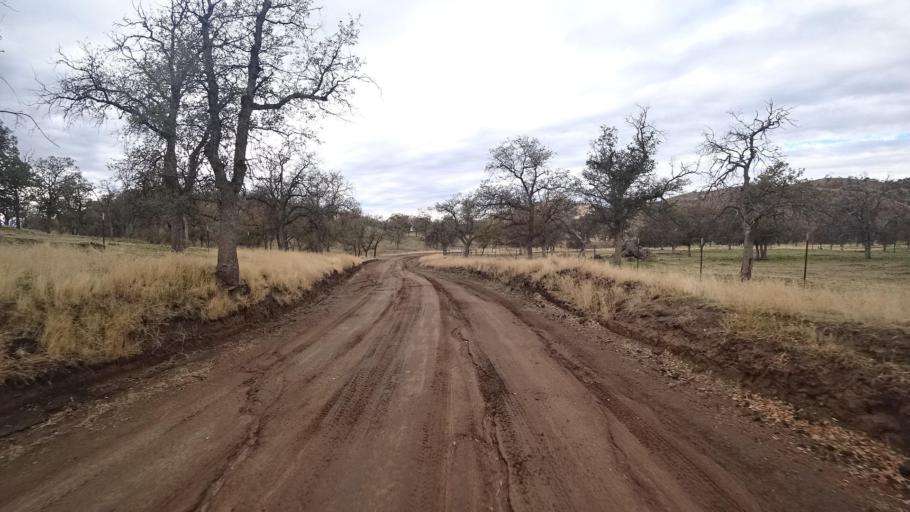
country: US
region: California
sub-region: Kern County
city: Stallion Springs
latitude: 35.1227
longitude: -118.7198
